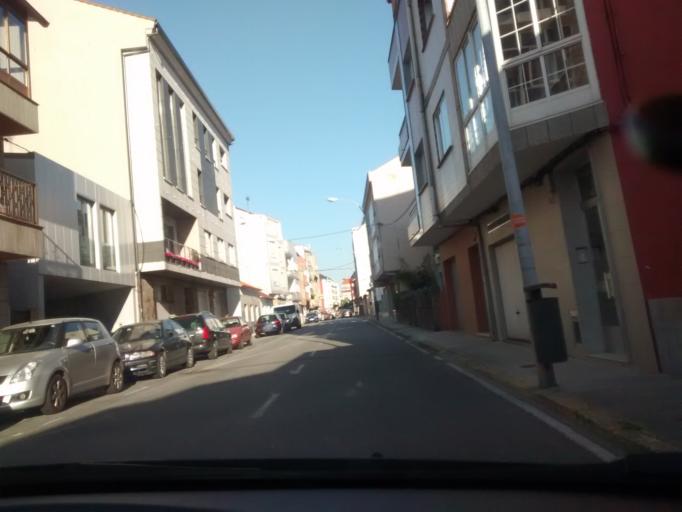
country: ES
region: Galicia
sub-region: Provincia de Pontevedra
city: O Grove
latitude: 42.4939
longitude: -8.8702
